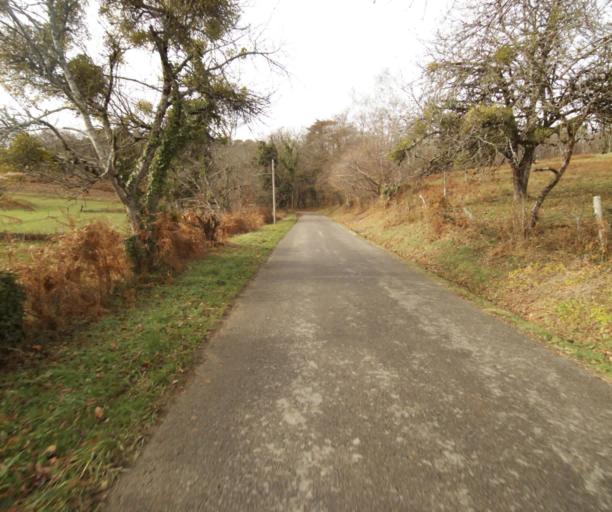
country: FR
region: Limousin
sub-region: Departement de la Correze
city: Chameyrat
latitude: 45.2581
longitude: 1.6891
